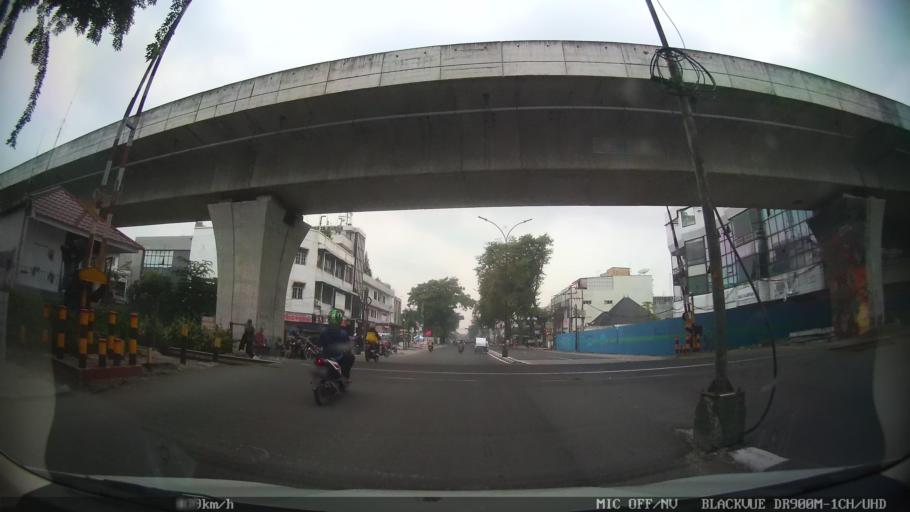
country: ID
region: North Sumatra
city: Medan
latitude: 3.5814
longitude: 98.6851
